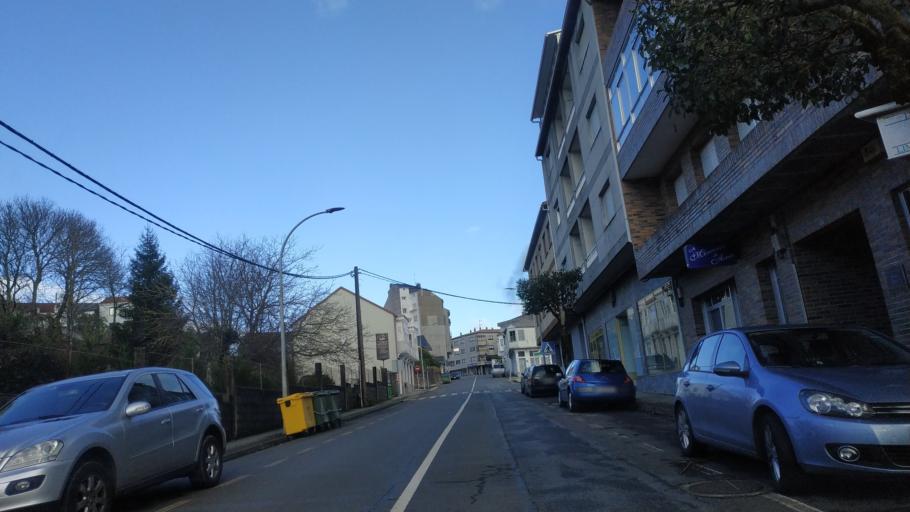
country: ES
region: Galicia
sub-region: Provincia de Pontevedra
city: Silleda
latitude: 42.7926
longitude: -8.1711
